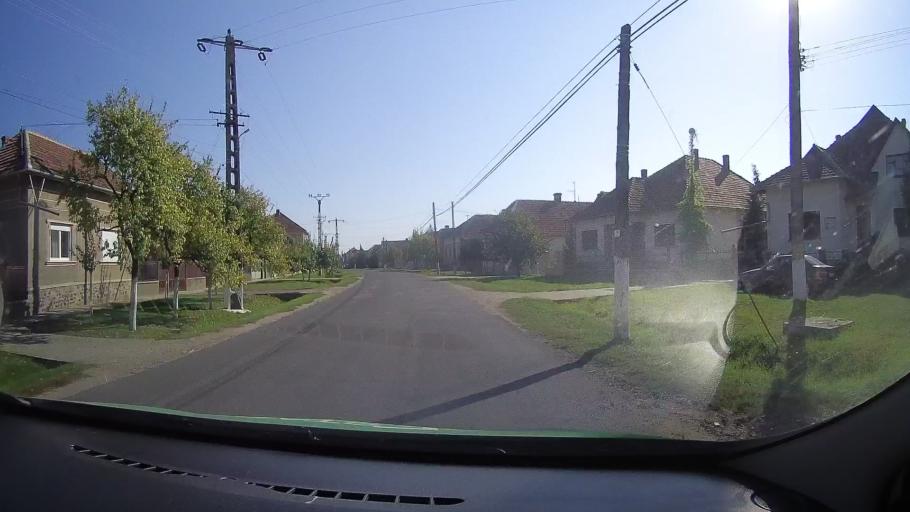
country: RO
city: Foieni
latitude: 47.6967
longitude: 22.3871
